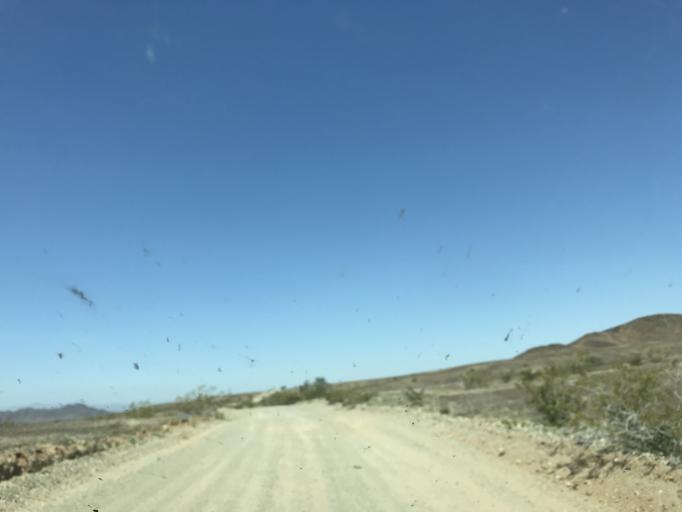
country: US
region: California
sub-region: Riverside County
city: Mesa Verde
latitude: 33.4979
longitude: -114.8466
